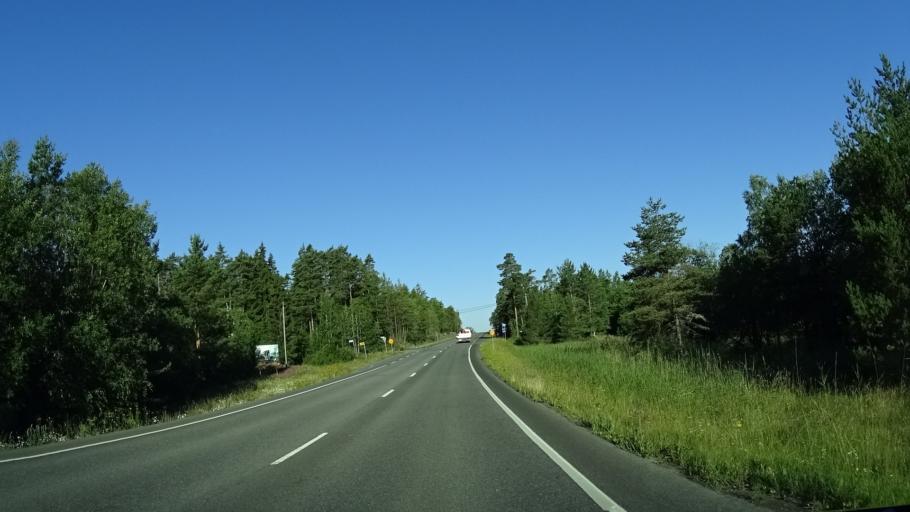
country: FI
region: Varsinais-Suomi
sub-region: Turku
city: Merimasku
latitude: 60.4607
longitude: 21.9363
